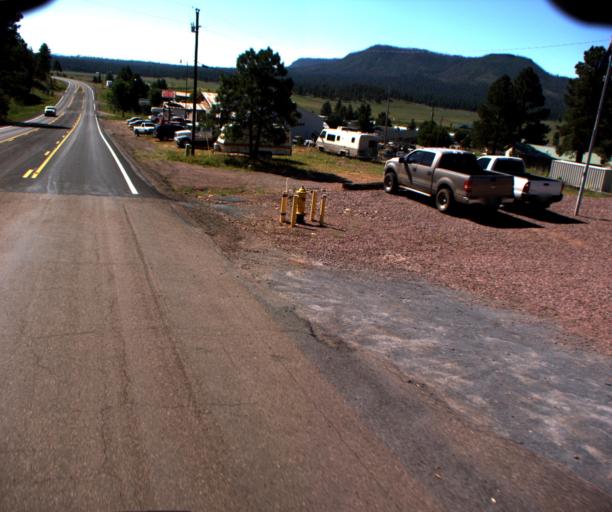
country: US
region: Arizona
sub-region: Apache County
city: Eagar
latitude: 33.8472
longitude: -109.1389
